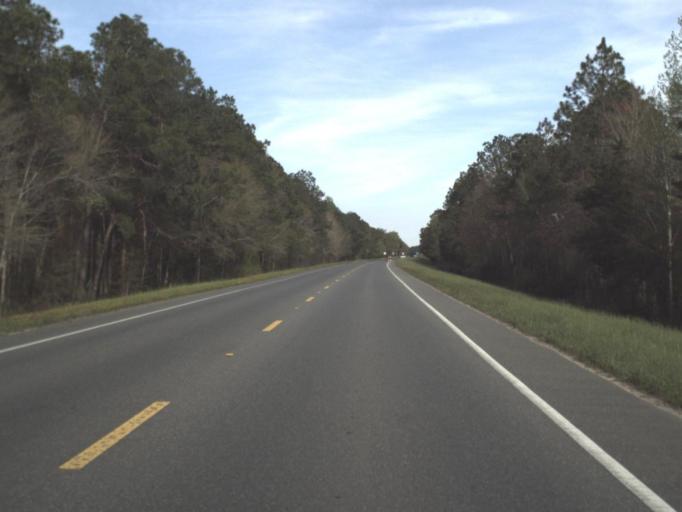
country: US
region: Florida
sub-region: Holmes County
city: Bonifay
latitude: 30.7792
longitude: -85.6246
